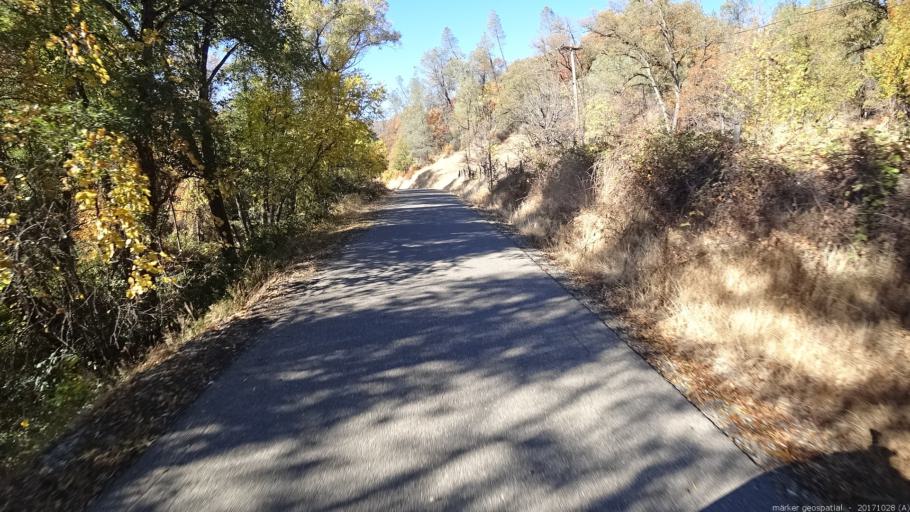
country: US
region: California
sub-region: Shasta County
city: Shasta
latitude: 40.7602
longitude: -122.6038
